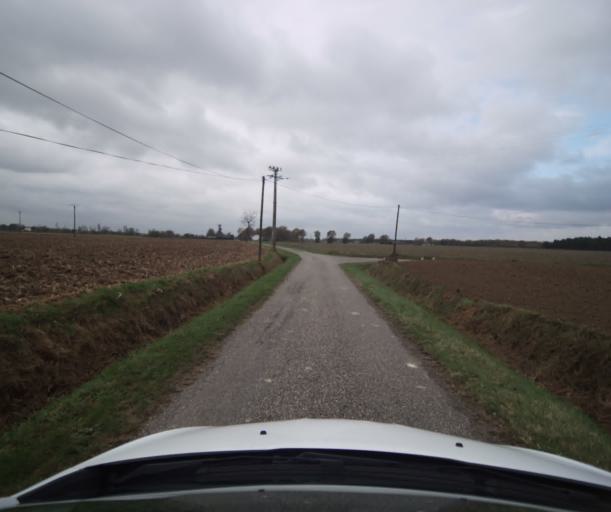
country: FR
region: Midi-Pyrenees
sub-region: Departement du Tarn-et-Garonne
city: Saint-Porquier
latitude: 44.0596
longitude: 1.1598
